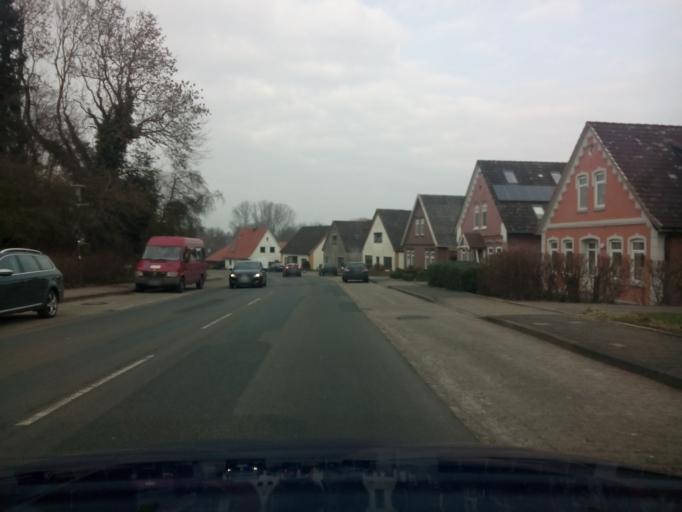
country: DE
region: Lower Saxony
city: Lintig
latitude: 53.6184
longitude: 8.8467
